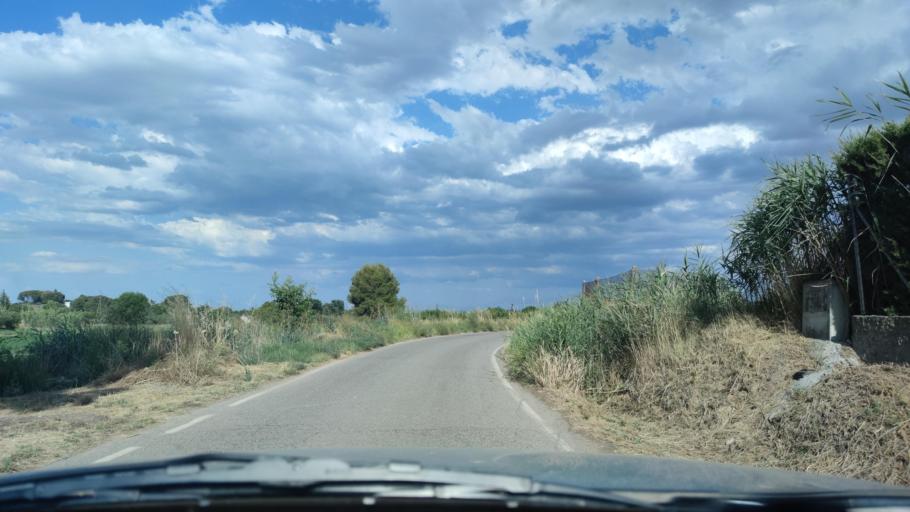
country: ES
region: Catalonia
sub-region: Provincia de Lleida
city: Alpicat
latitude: 41.6274
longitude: 0.5741
